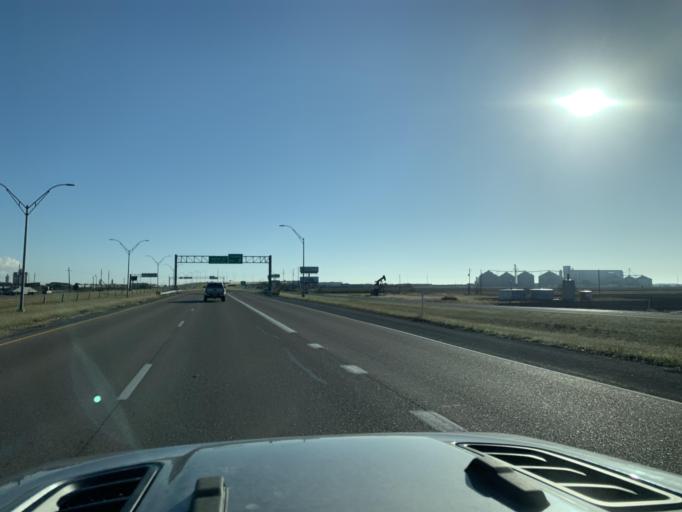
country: US
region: Texas
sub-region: Nueces County
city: Corpus Christi
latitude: 27.7848
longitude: -97.4949
